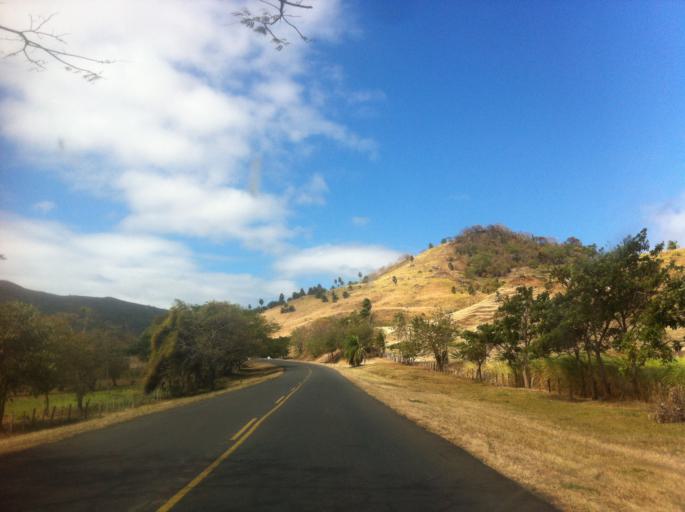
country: NI
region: Chontales
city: Acoyapa
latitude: 12.0016
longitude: -85.2011
